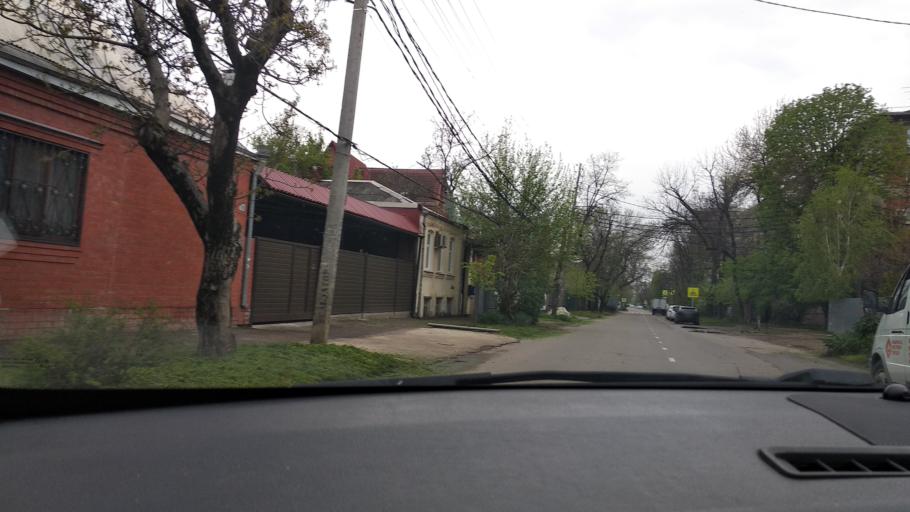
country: RU
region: Krasnodarskiy
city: Krasnodar
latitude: 45.0323
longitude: 38.9865
